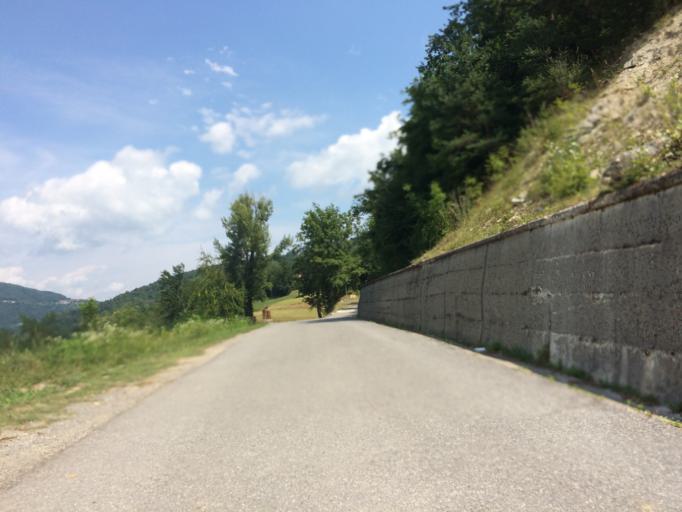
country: IT
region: Piedmont
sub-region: Provincia di Cuneo
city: Bagnasco
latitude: 44.3092
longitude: 8.0567
